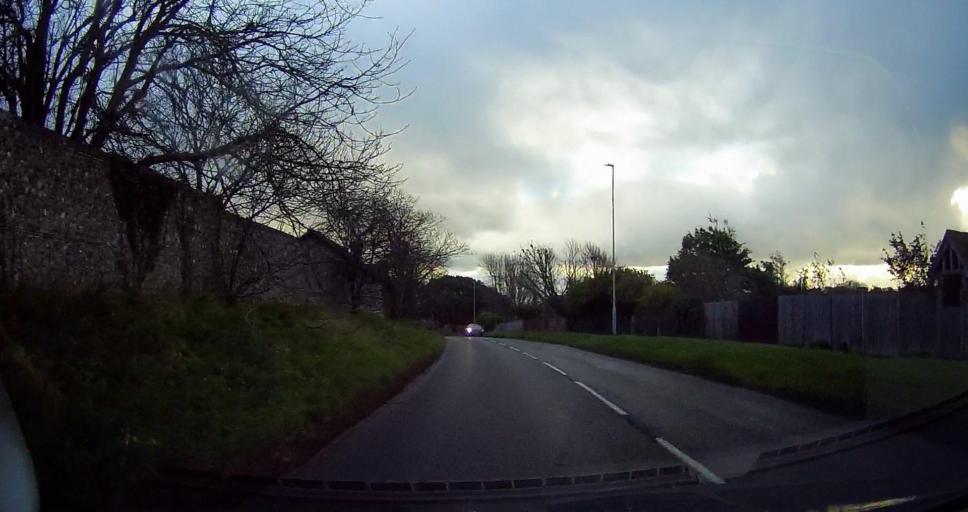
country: GB
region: England
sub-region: Brighton and Hove
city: Rottingdean
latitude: 50.8168
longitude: -0.0643
